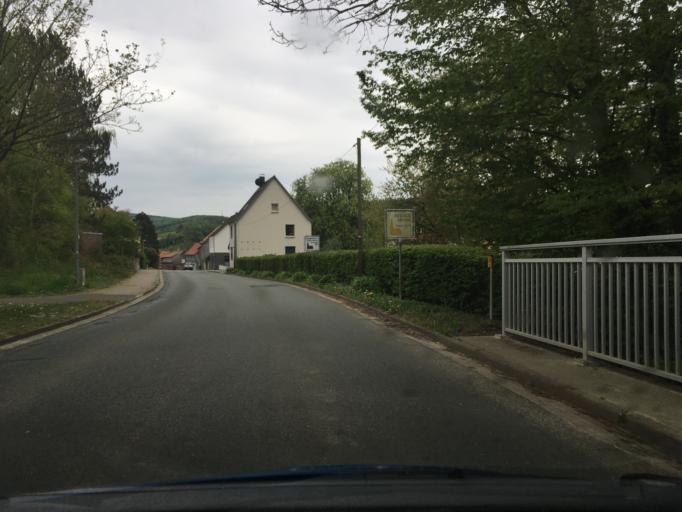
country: DE
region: Lower Saxony
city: Delligsen
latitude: 51.9468
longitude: 9.7967
